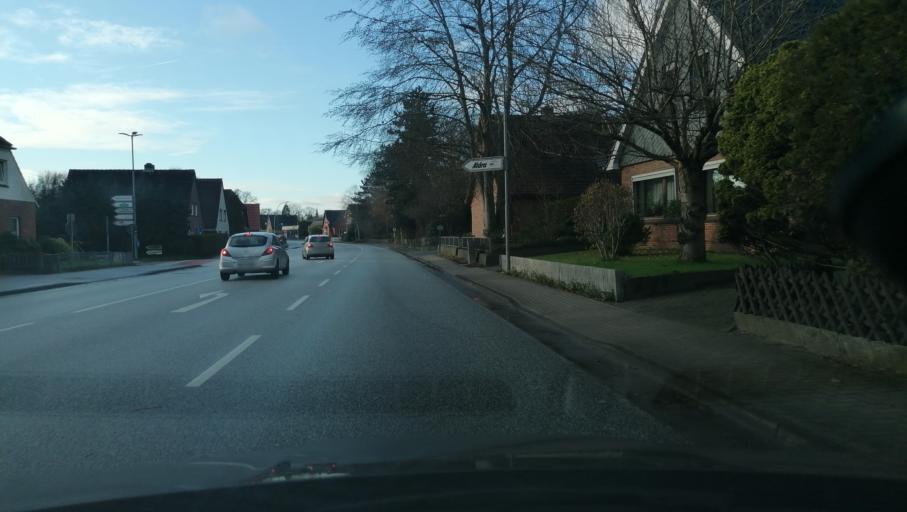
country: DE
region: Schleswig-Holstein
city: Nindorf
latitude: 54.0891
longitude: 9.0942
